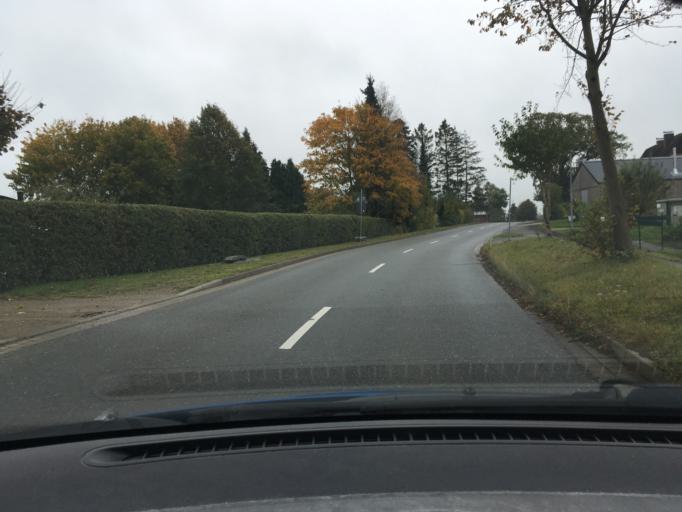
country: DE
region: Schleswig-Holstein
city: Bosdorf
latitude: 54.1233
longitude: 10.4754
